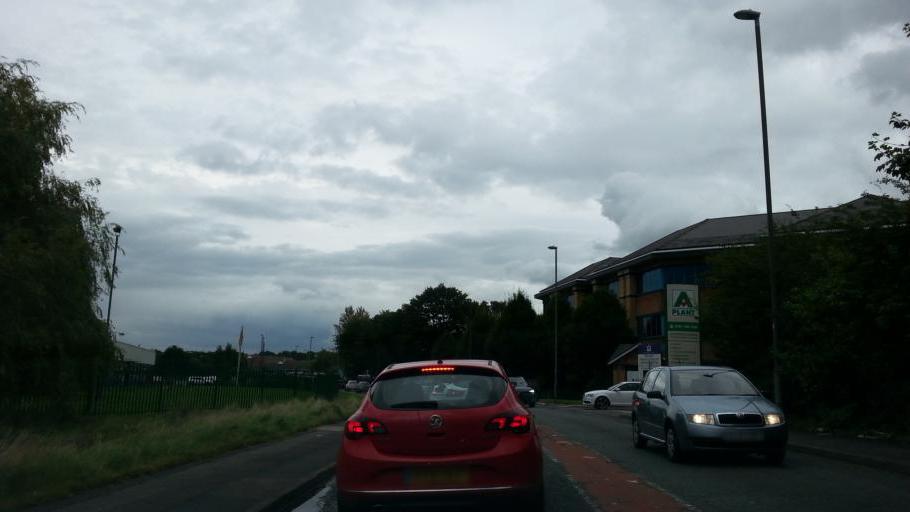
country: GB
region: England
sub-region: Borough of Bury
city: Whitefield
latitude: 53.5749
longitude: -2.2802
